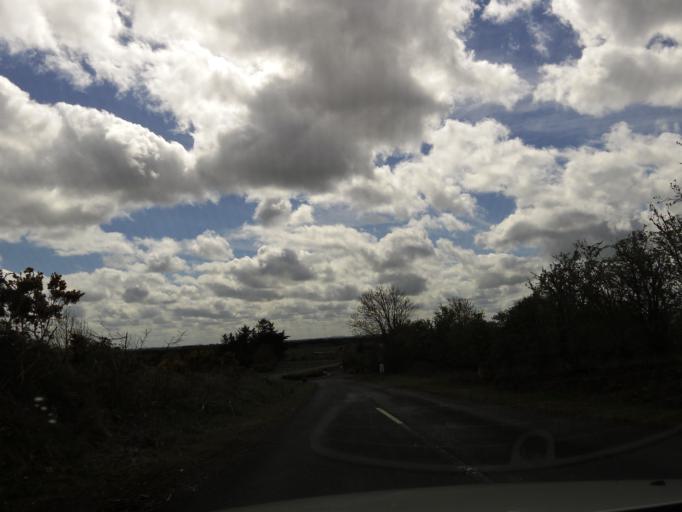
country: IE
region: Connaught
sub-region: Maigh Eo
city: Claremorris
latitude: 53.7568
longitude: -8.9649
